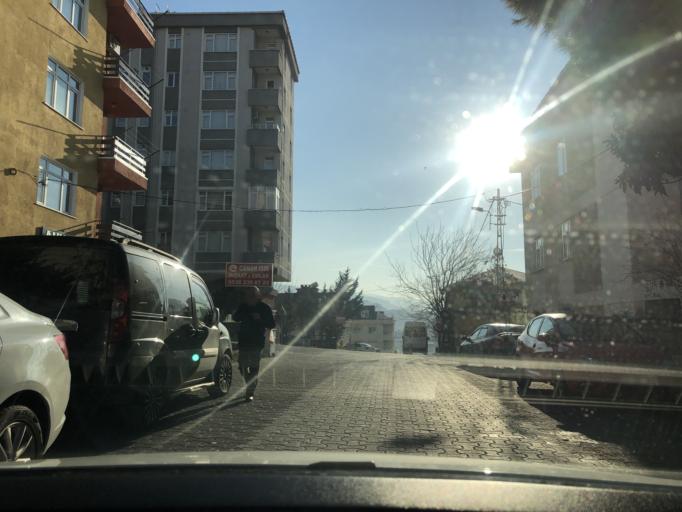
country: TR
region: Istanbul
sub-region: Atasehir
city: Atasehir
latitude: 40.9727
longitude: 29.1214
